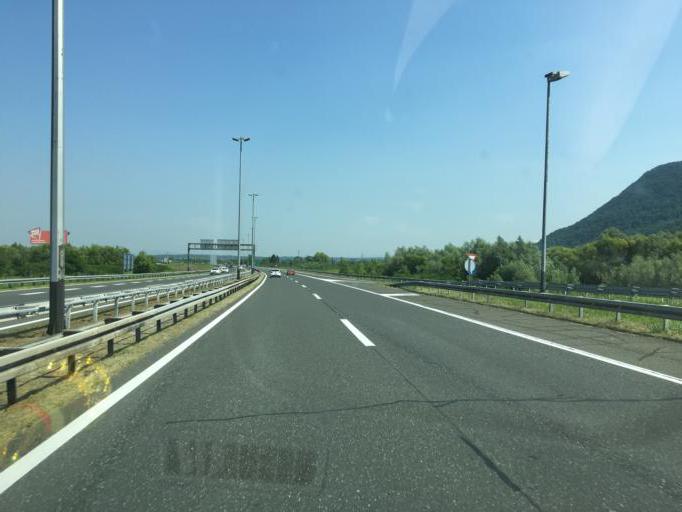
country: HR
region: Zagrebacka
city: Zapresic
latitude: 45.8572
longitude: 15.8294
